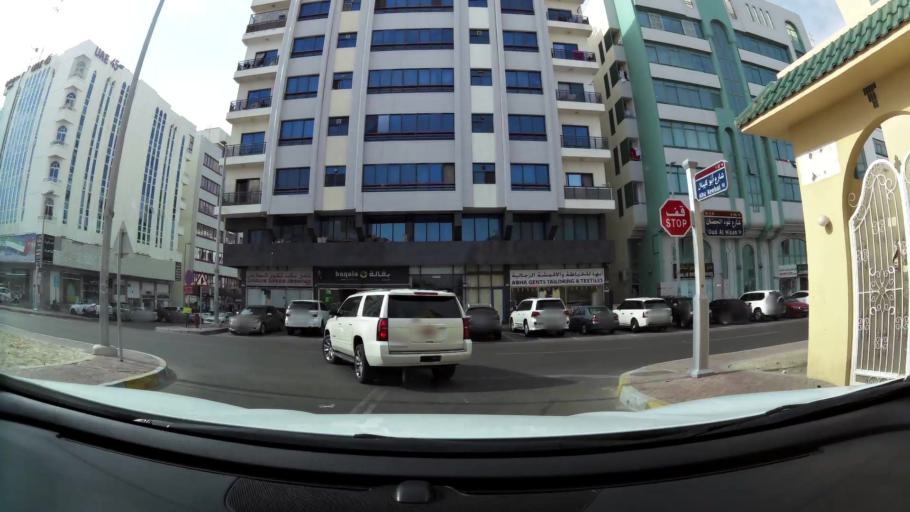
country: AE
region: Abu Dhabi
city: Abu Dhabi
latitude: 24.4692
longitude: 54.3476
